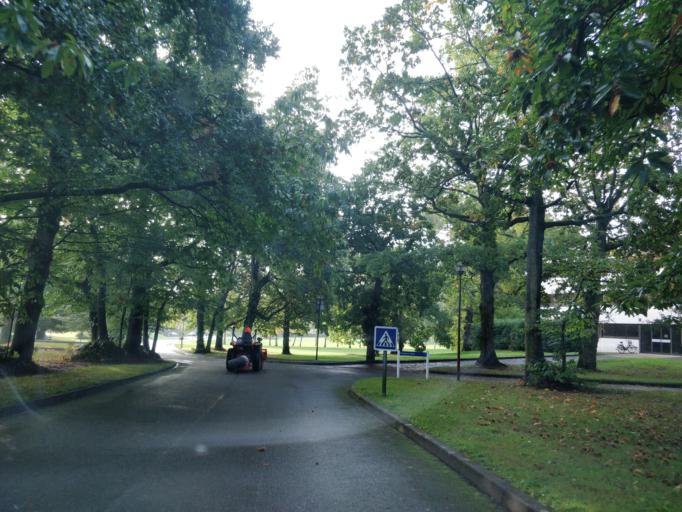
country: FR
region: Brittany
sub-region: Departement d'Ille-et-Vilaine
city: Cesson-Sevigne
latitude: 48.1252
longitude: -1.6250
